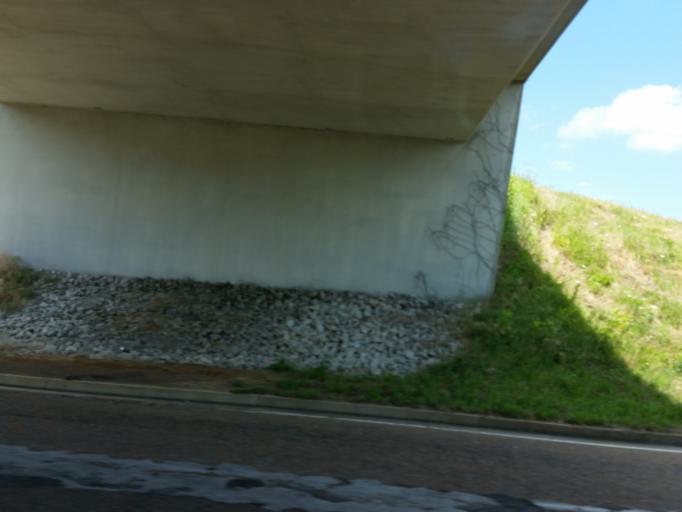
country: US
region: Tennessee
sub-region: Weakley County
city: Martin
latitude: 36.3706
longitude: -88.8507
